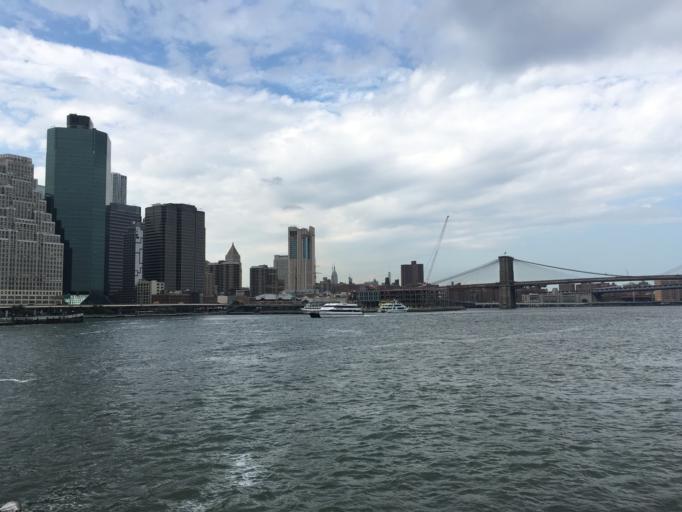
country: US
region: New York
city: New York City
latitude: 40.6999
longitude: -74.0047
